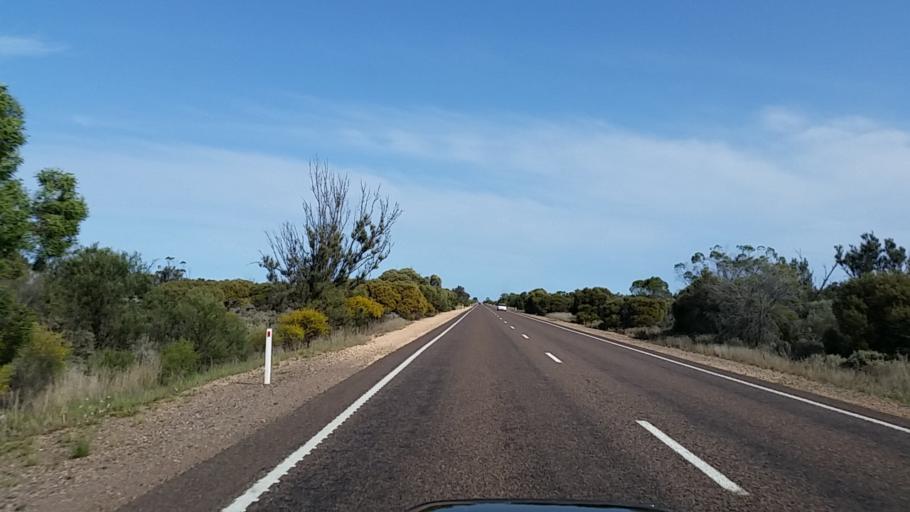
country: AU
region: South Australia
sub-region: Whyalla
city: Whyalla
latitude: -32.8958
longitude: 137.5615
